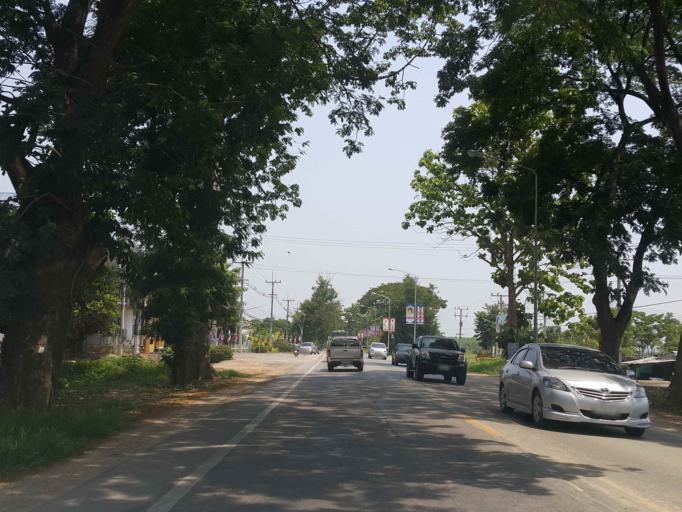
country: TH
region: Chiang Mai
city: Mae Taeng
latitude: 19.0136
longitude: 98.9711
